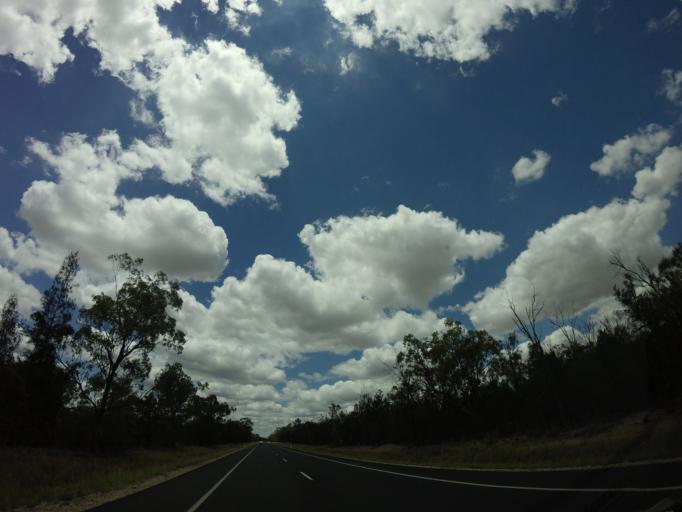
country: AU
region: Queensland
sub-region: Goondiwindi
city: Goondiwindi
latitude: -28.0704
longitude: 150.7519
